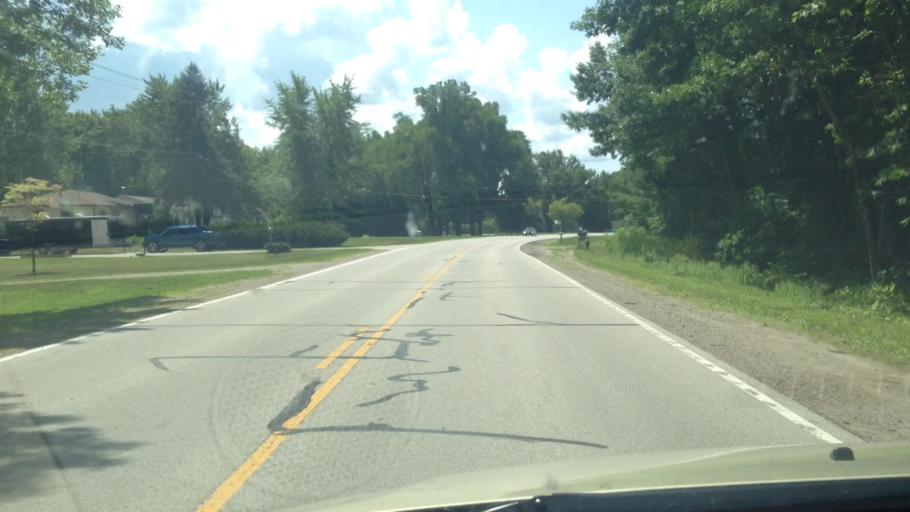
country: US
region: Wisconsin
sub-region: Brown County
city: Suamico
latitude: 44.6388
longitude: -88.0497
